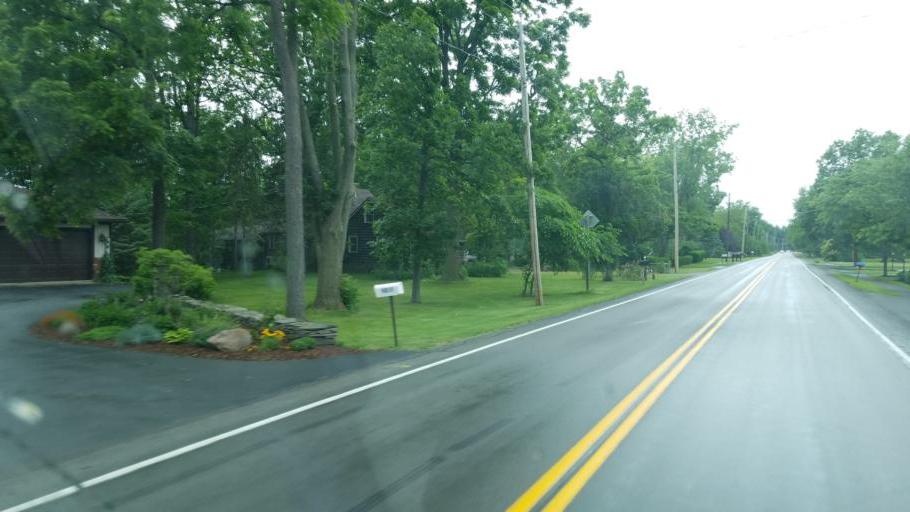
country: US
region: New York
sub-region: Niagara County
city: Lewiston
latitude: 43.2044
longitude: -79.0438
